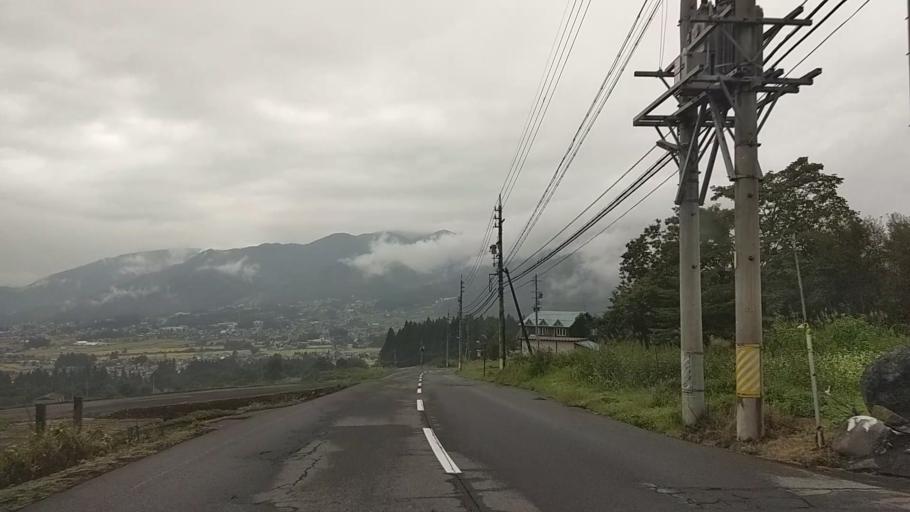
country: JP
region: Nagano
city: Iiyama
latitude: 36.8271
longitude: 138.3996
